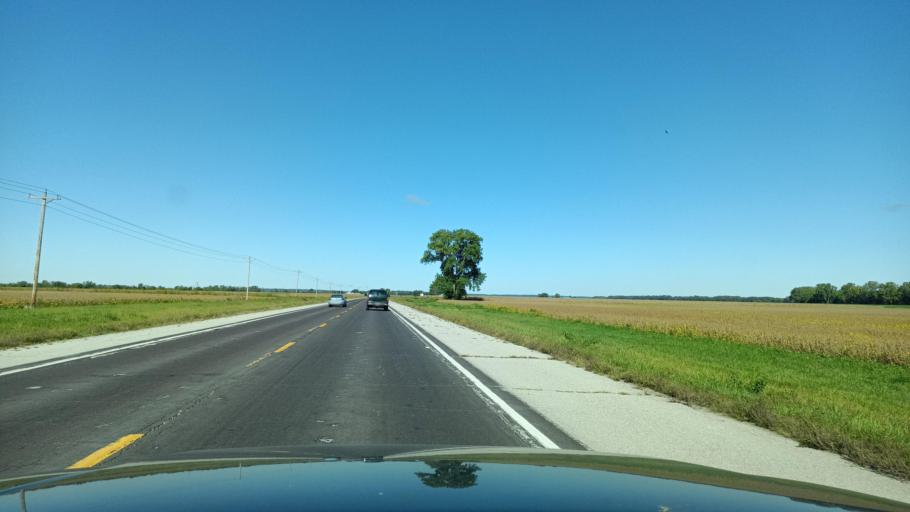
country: US
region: Illinois
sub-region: Hancock County
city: Warsaw
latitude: 40.3742
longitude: -91.4859
